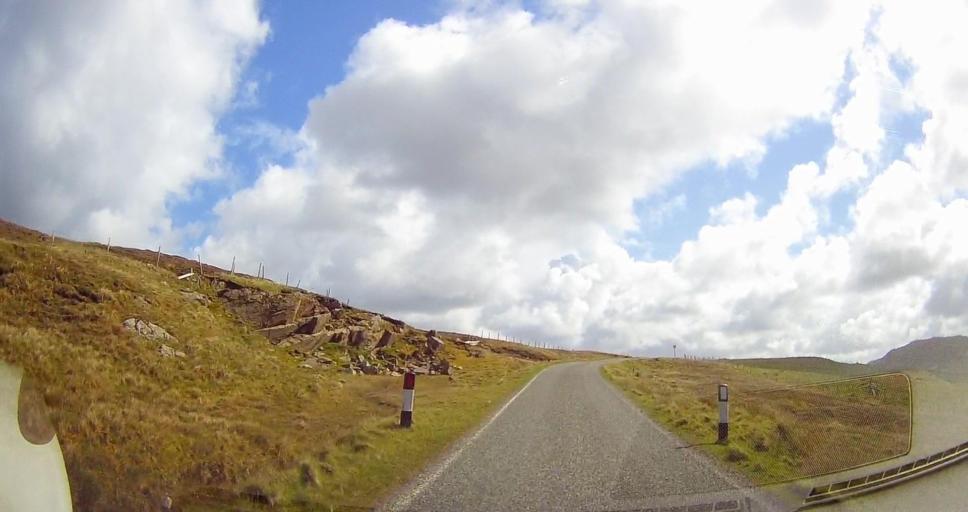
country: GB
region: Scotland
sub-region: Shetland Islands
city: Lerwick
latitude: 60.5633
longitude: -1.3341
